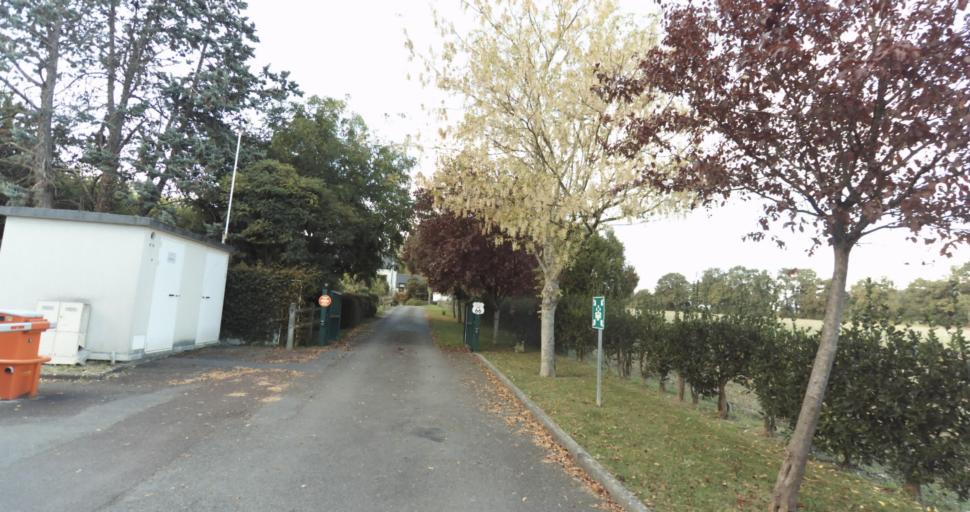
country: FR
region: Brittany
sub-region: Departement d'Ille-et-Vilaine
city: Cesson-Sevigne
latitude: 48.1331
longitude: -1.6335
